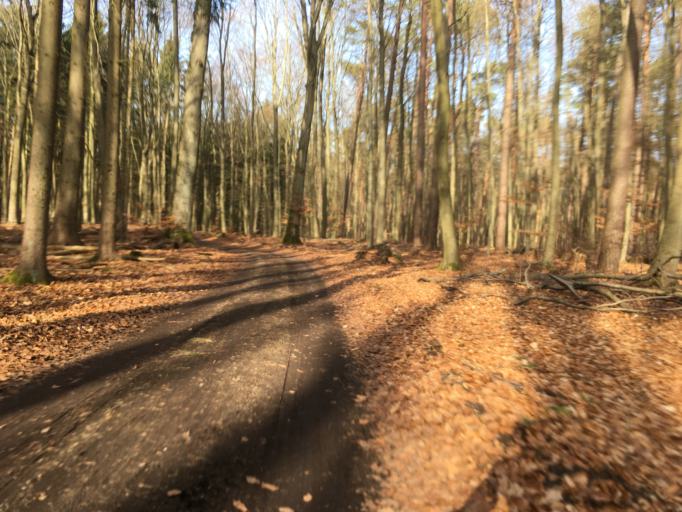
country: DE
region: Brandenburg
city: Wandlitz
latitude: 52.7370
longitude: 13.5236
